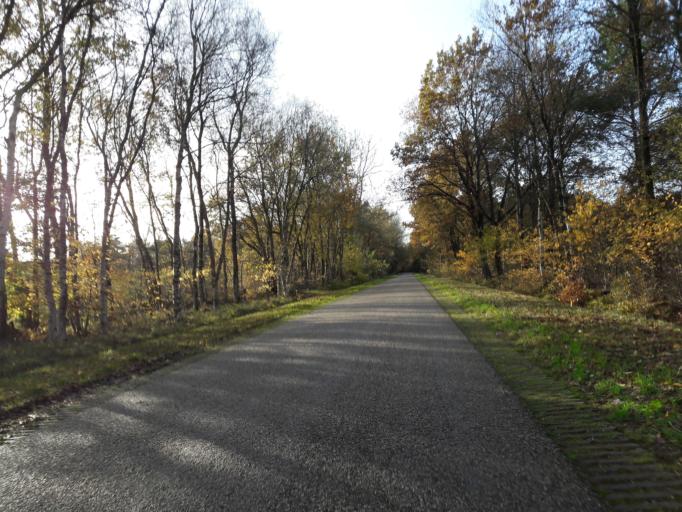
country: NL
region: Drenthe
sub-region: Gemeente Aa en Hunze
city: Anloo
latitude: 52.9416
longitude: 6.6891
